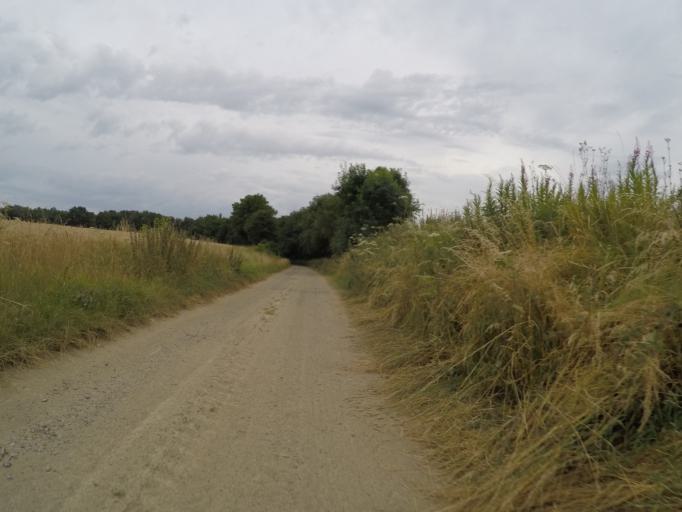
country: BE
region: Wallonia
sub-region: Province de Namur
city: Assesse
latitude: 50.3015
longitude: 5.0134
